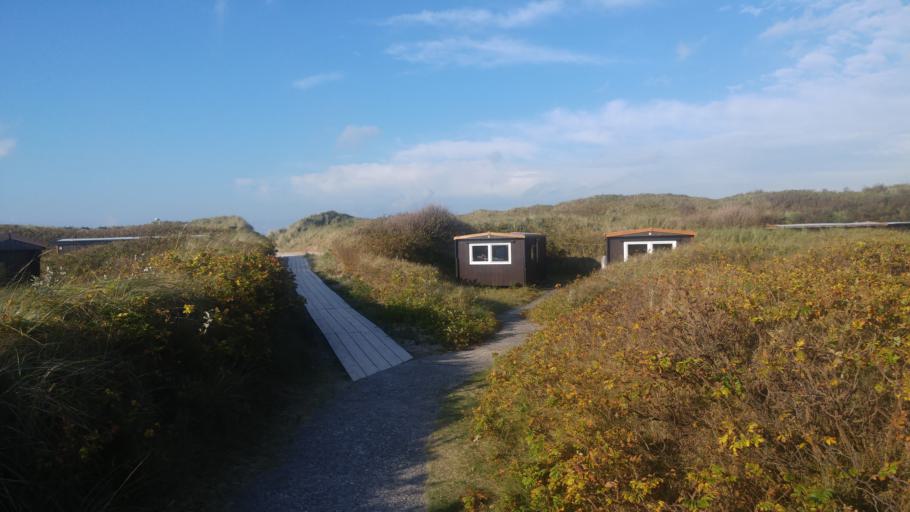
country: DE
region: Schleswig-Holstein
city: Helgoland
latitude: 54.1875
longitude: 7.9135
